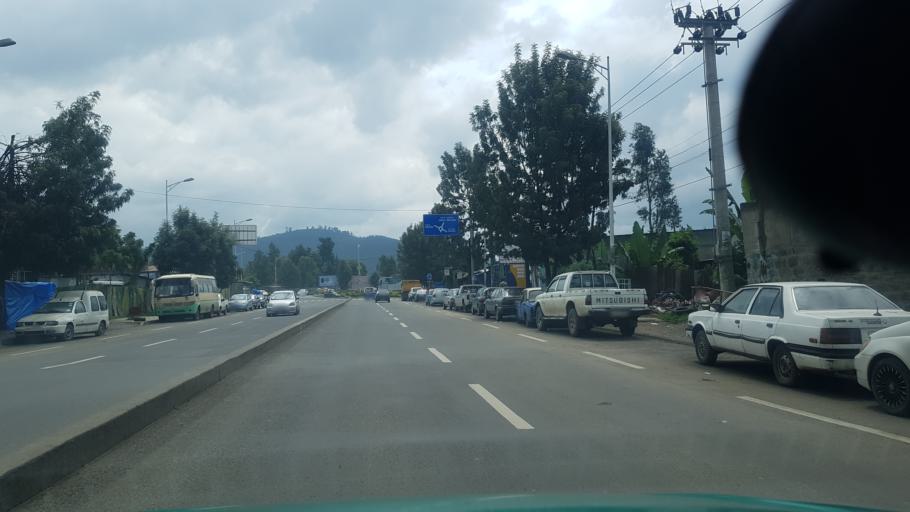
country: ET
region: Adis Abeba
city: Addis Ababa
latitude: 9.0225
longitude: 38.7751
